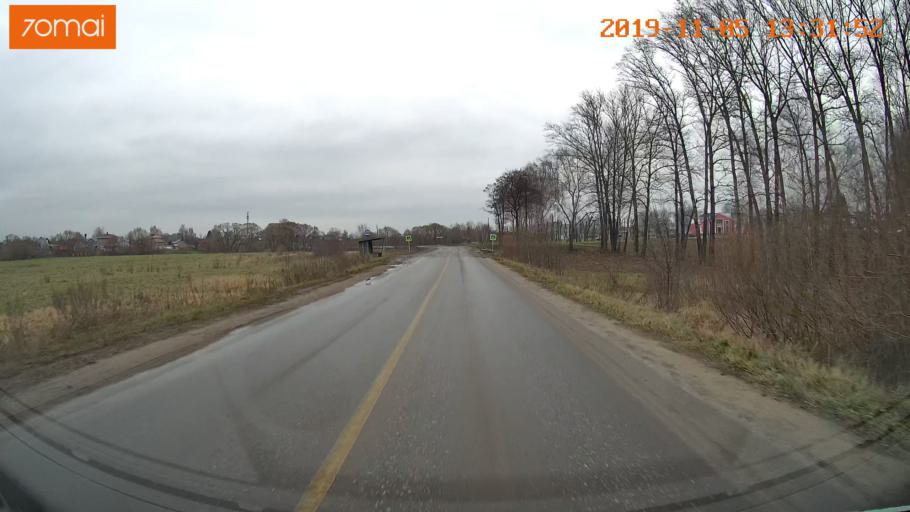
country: RU
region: Ivanovo
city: Shuya
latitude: 56.8791
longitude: 41.3964
